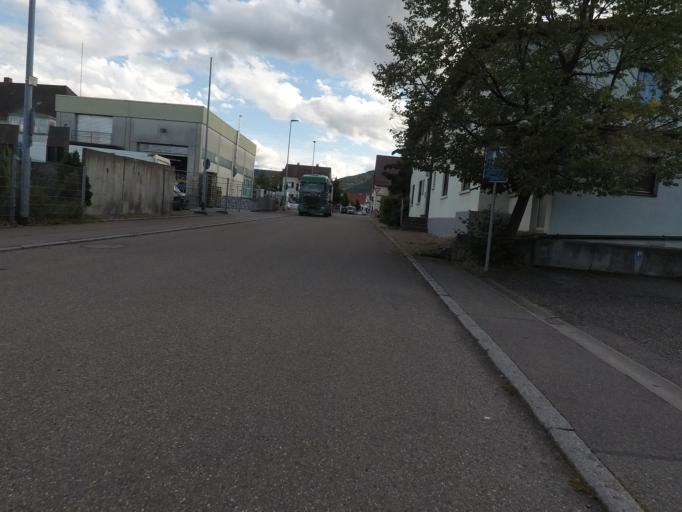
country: DE
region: Baden-Wuerttemberg
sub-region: Tuebingen Region
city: Pfullingen
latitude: 48.4735
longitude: 9.2263
